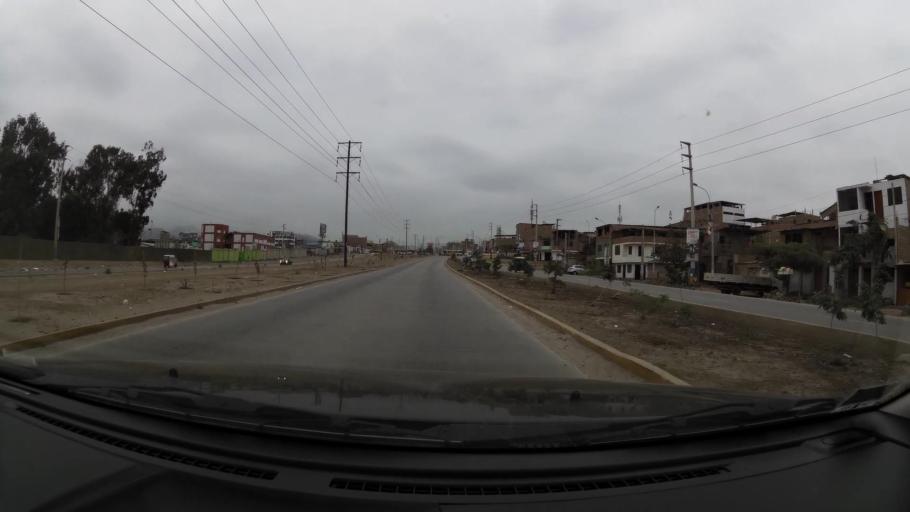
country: PE
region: Lima
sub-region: Lima
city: Surco
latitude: -12.2071
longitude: -76.9552
